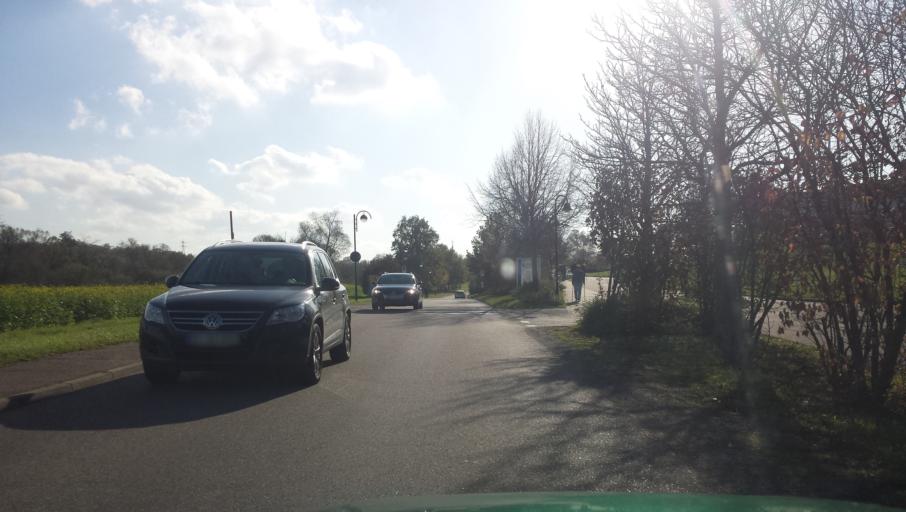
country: DE
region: Baden-Wuerttemberg
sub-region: Karlsruhe Region
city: Malsch
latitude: 49.2174
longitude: 8.6725
